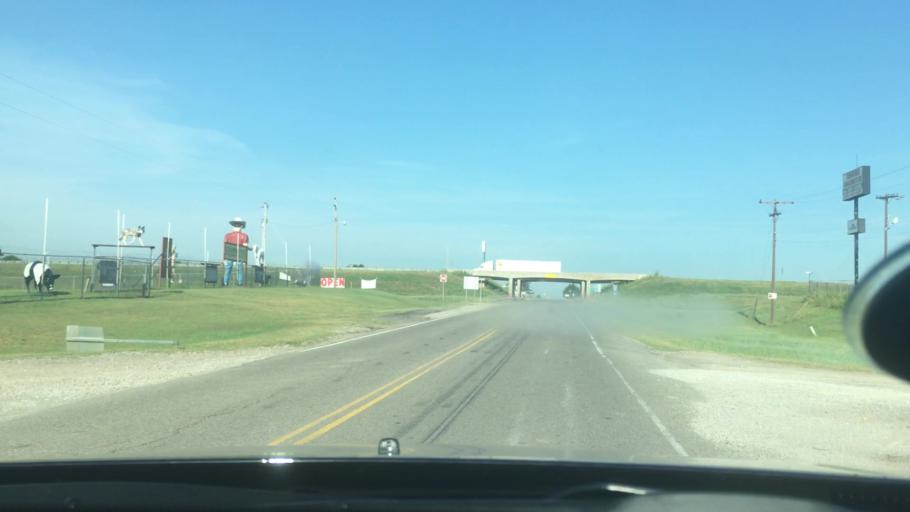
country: US
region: Oklahoma
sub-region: Garvin County
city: Wynnewood
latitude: 34.6517
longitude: -97.2181
